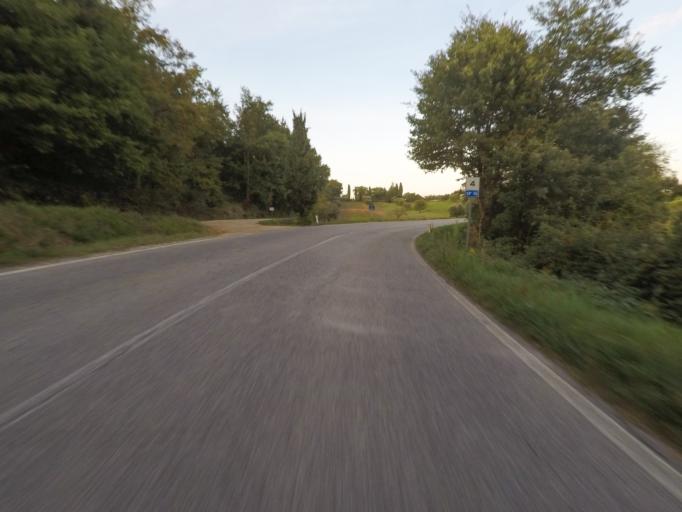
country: IT
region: Tuscany
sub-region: Provincia di Siena
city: Torrita di Siena
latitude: 43.1388
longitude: 11.7331
